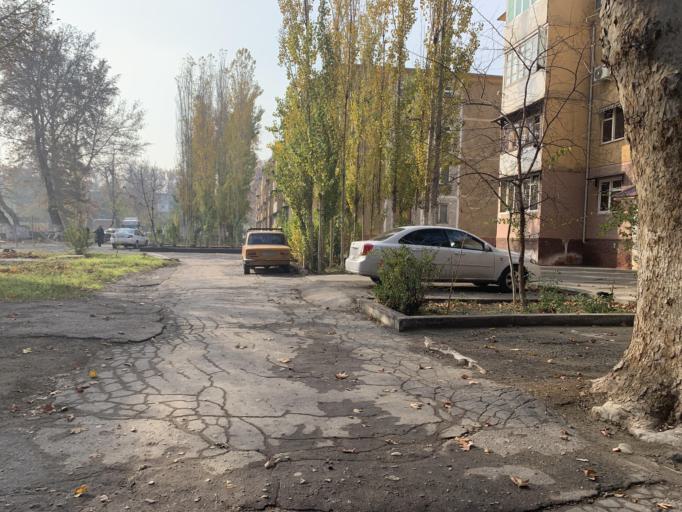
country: UZ
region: Fergana
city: Qo`qon
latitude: 40.5475
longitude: 70.9244
